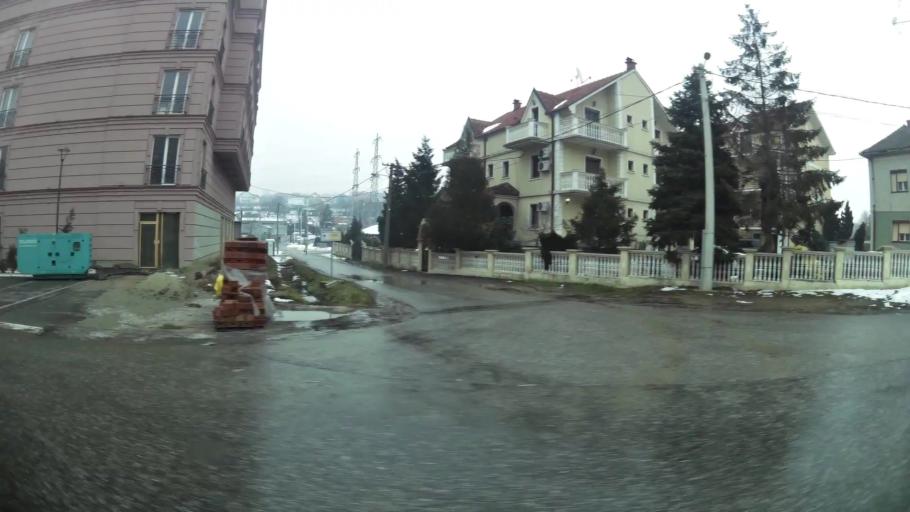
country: RS
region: Central Serbia
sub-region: Belgrade
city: Zvezdara
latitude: 44.7744
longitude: 20.5114
